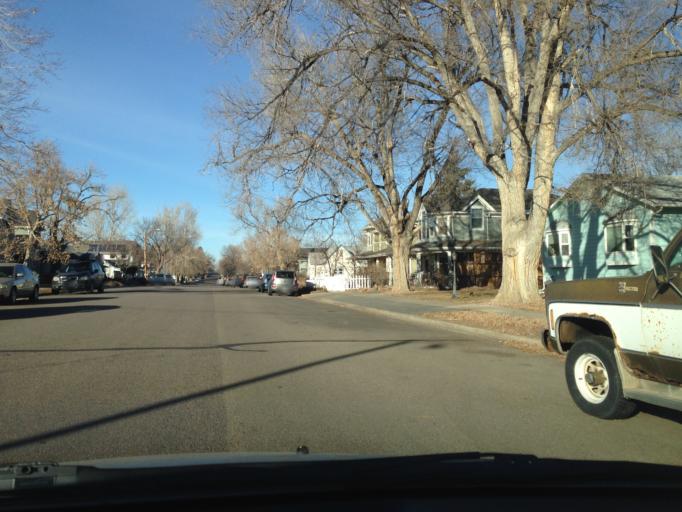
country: US
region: Colorado
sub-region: Boulder County
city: Louisville
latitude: 39.9748
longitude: -105.1345
